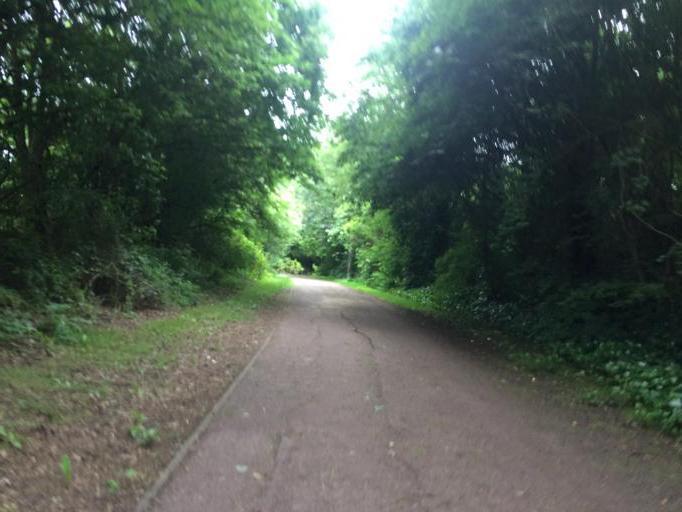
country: GB
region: England
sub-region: Milton Keynes
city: Loughton
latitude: 52.0311
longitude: -0.7723
